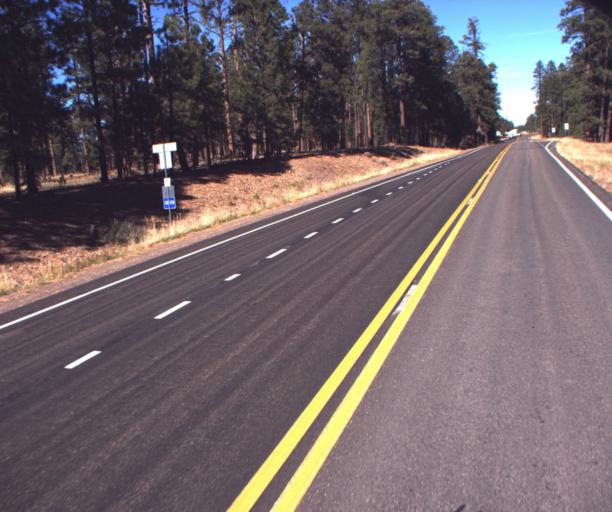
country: US
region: Arizona
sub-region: Coconino County
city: Fredonia
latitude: 36.7099
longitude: -112.2176
